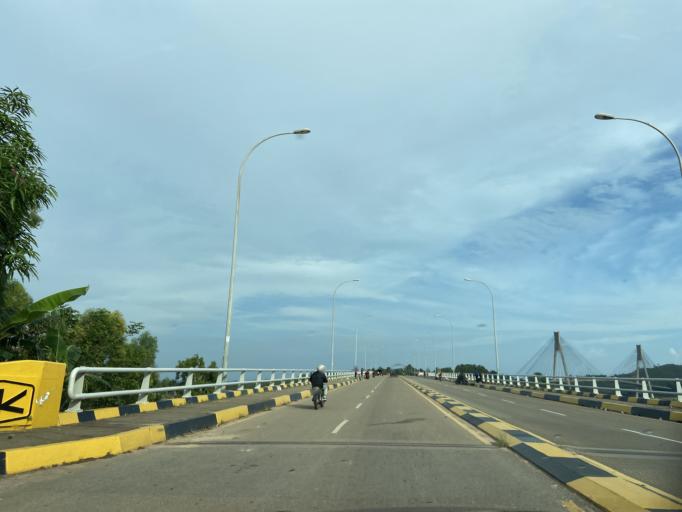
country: SG
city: Singapore
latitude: 0.9761
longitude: 104.0514
